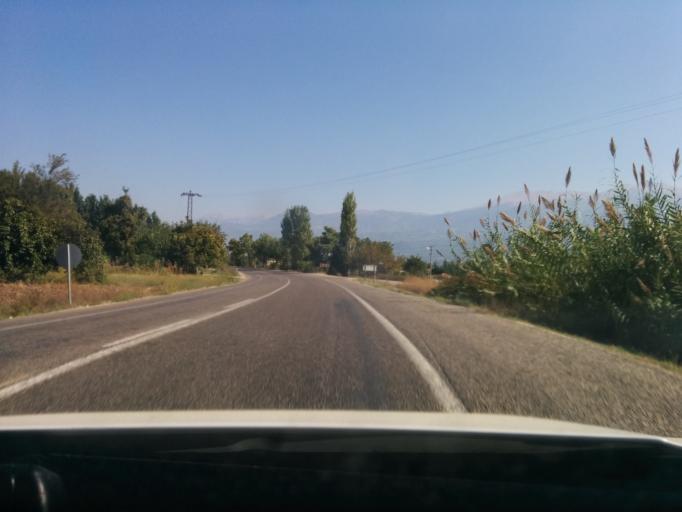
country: TR
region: Mugla
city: Esen
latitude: 36.5066
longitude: 29.3306
